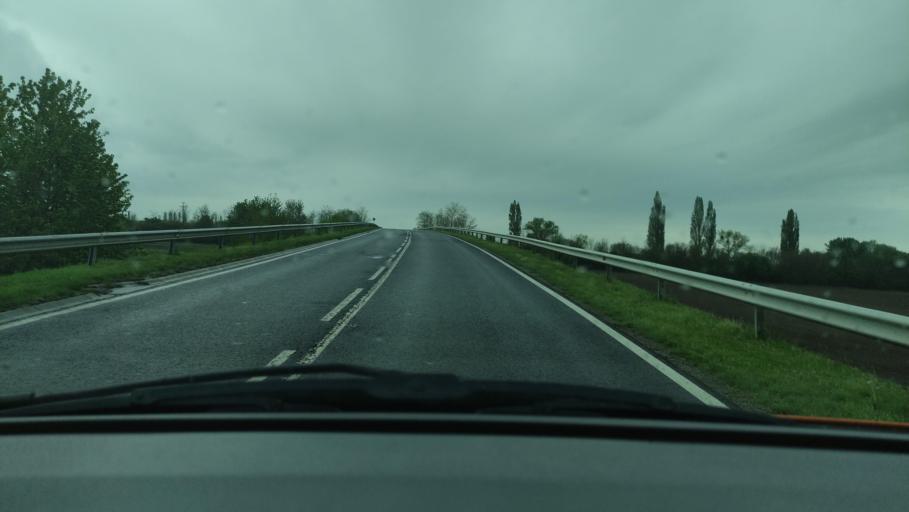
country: HU
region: Baranya
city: Mohacs
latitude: 45.9921
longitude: 18.6552
